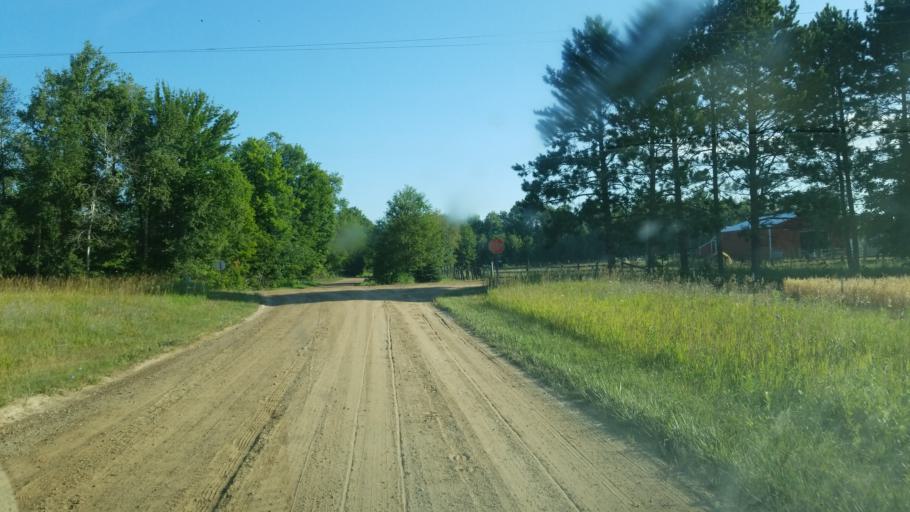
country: US
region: Michigan
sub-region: Mecosta County
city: Canadian Lakes
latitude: 43.5544
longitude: -85.4231
